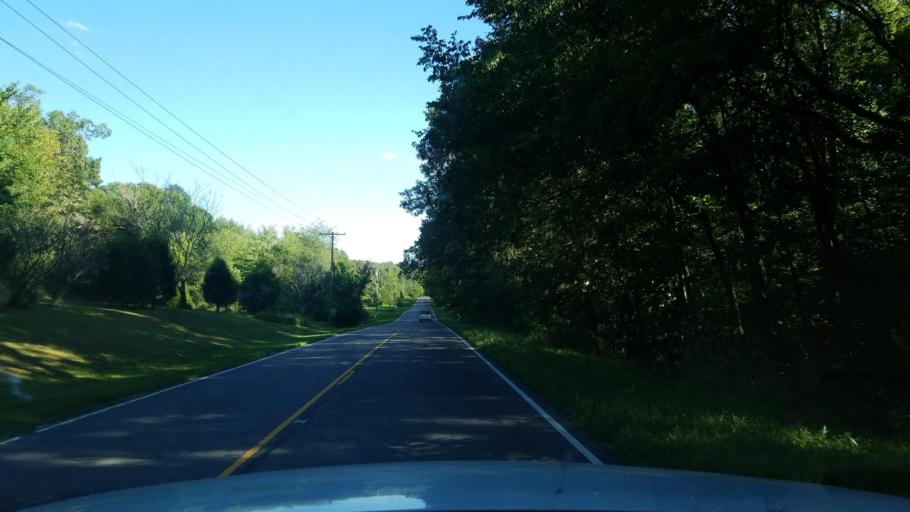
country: US
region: Illinois
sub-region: Saline County
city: Harrisburg
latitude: 37.6145
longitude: -88.4670
